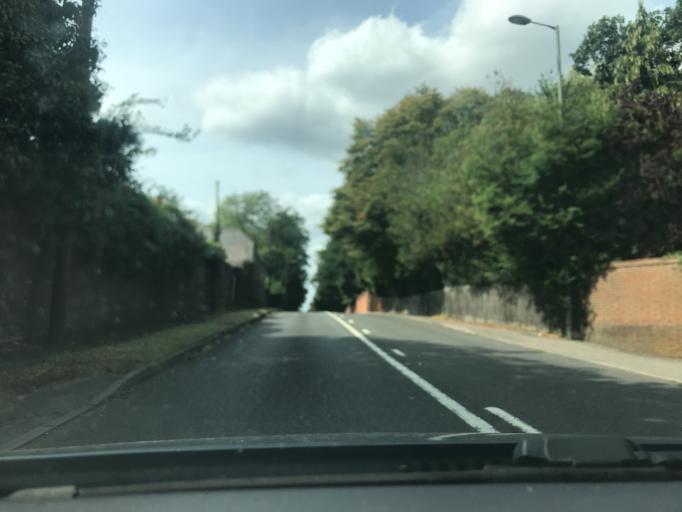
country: GB
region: England
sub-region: Surrey
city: Addlestone
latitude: 51.3786
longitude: -0.4850
